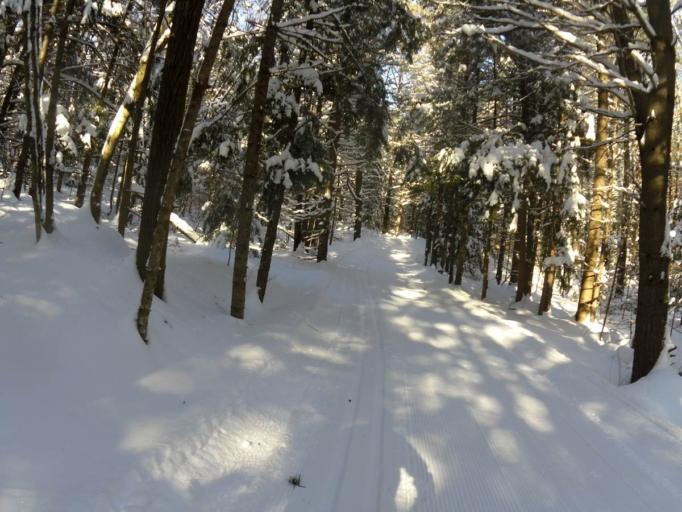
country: CA
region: Quebec
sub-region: Outaouais
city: Wakefield
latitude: 45.6251
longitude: -75.9484
